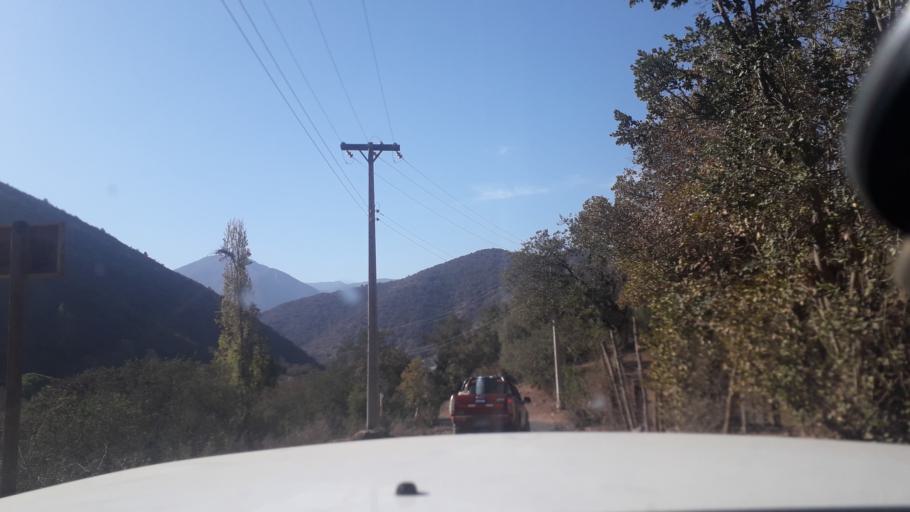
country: CL
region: Valparaiso
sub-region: Provincia de Marga Marga
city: Limache
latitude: -33.0725
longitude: -71.0999
